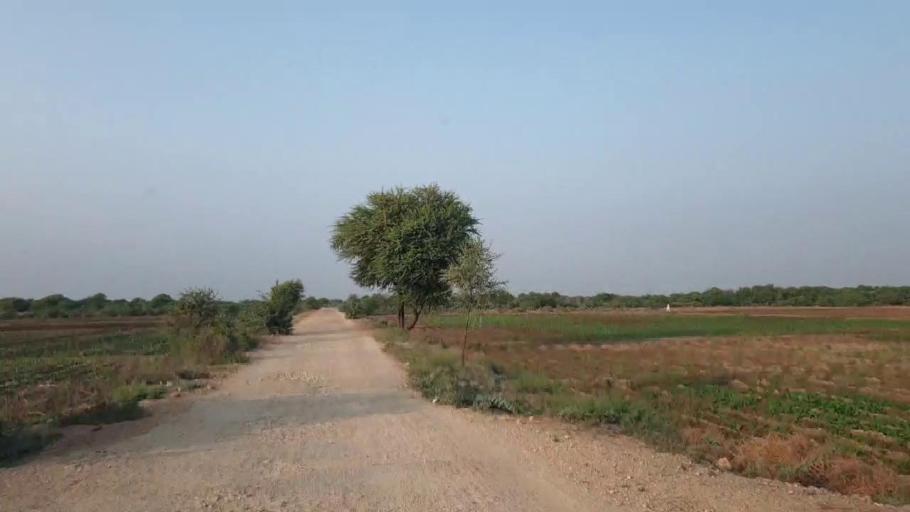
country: PK
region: Sindh
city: Rajo Khanani
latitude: 25.0312
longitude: 68.9773
